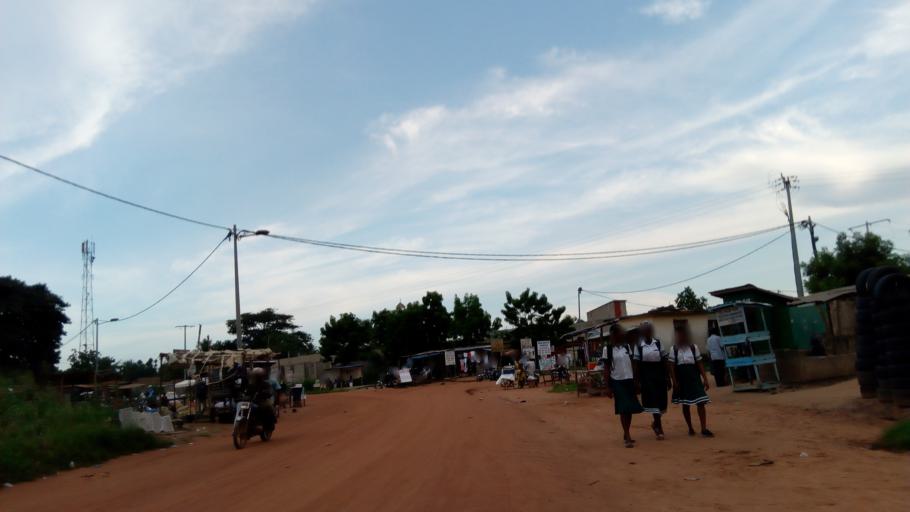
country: TG
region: Maritime
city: Lome
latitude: 6.2486
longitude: 1.1399
